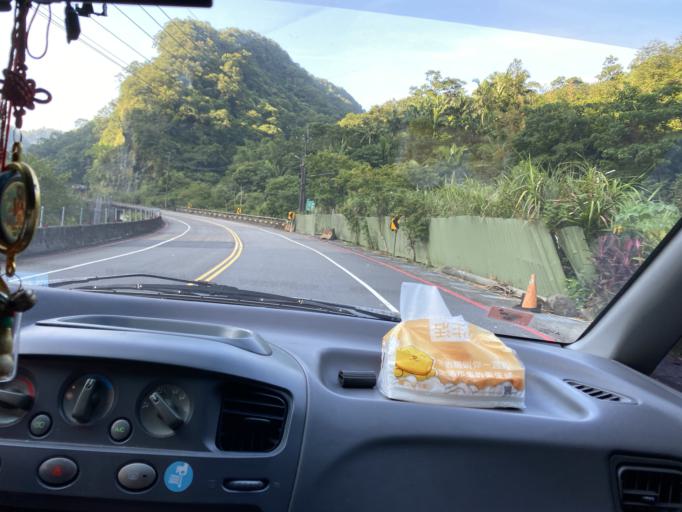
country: TW
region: Taiwan
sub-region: Keelung
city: Keelung
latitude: 25.0377
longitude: 121.7795
